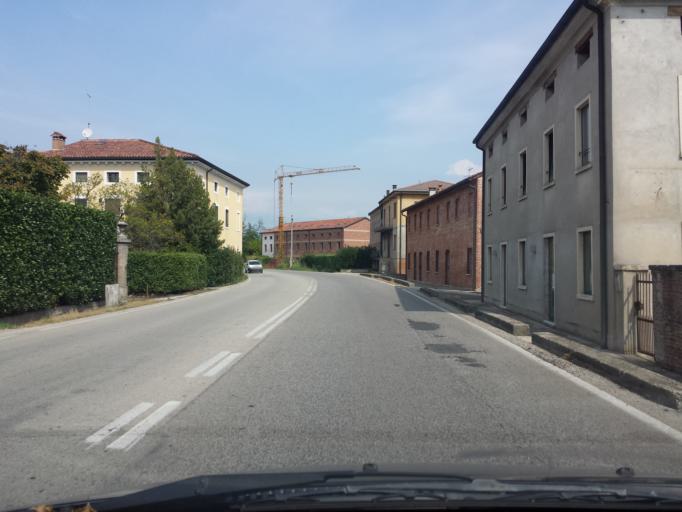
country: IT
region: Veneto
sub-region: Provincia di Vicenza
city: Monticello Conte Otto
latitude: 45.5983
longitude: 11.5571
